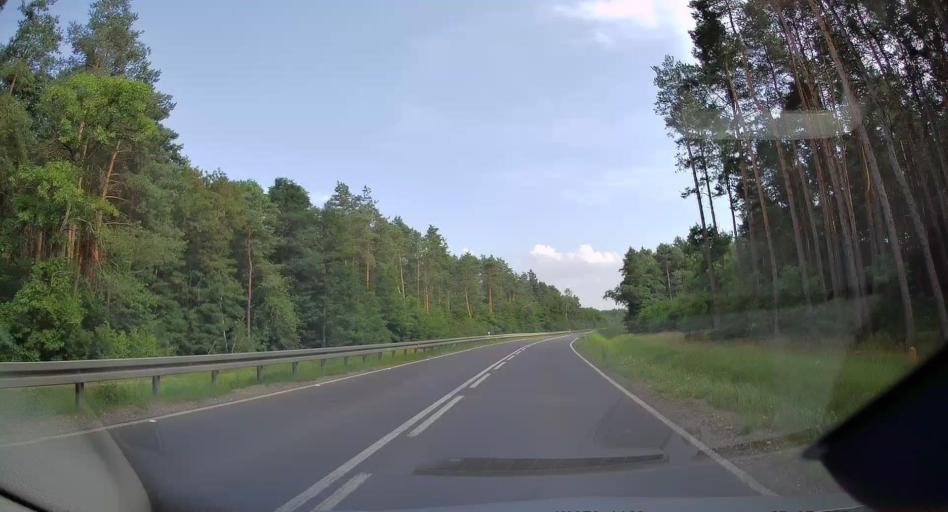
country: PL
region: Lodz Voivodeship
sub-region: Powiat tomaszowski
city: Inowlodz
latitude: 51.5107
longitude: 20.2325
